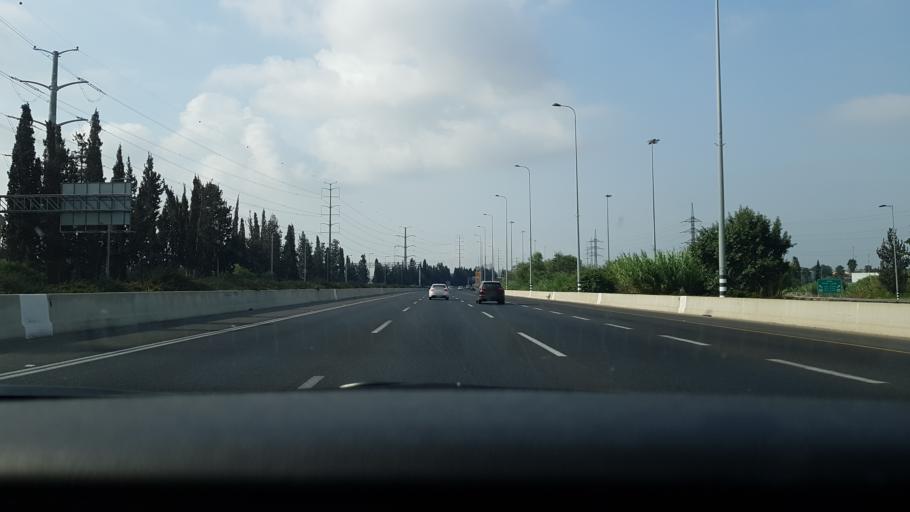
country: IL
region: Central District
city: Bet Dagan
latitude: 32.0049
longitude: 34.8104
